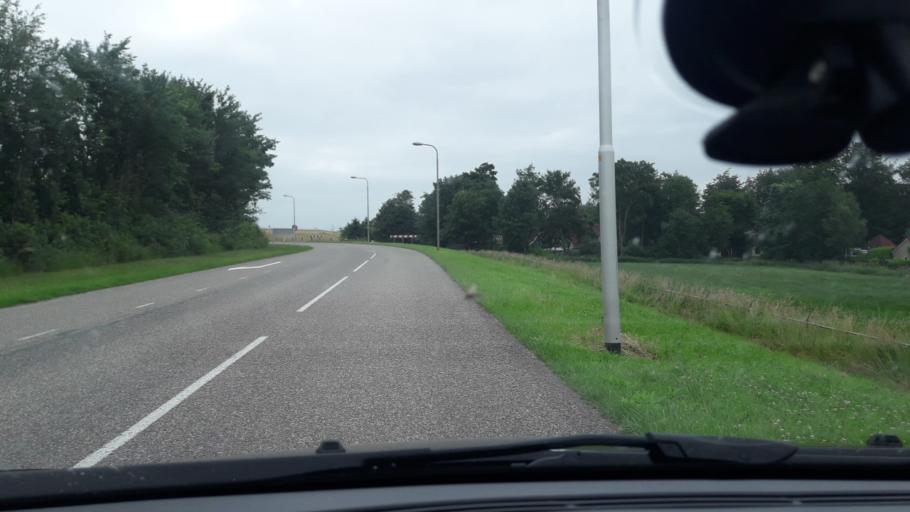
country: NL
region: Flevoland
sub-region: Gemeente Dronten
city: Dronten
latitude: 52.5785
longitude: 5.7612
